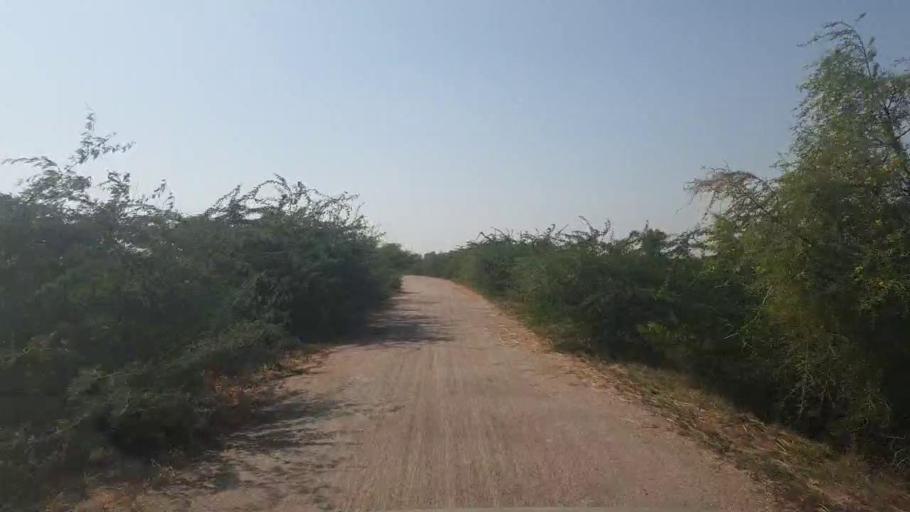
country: PK
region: Sindh
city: Badin
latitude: 24.5574
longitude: 68.8433
